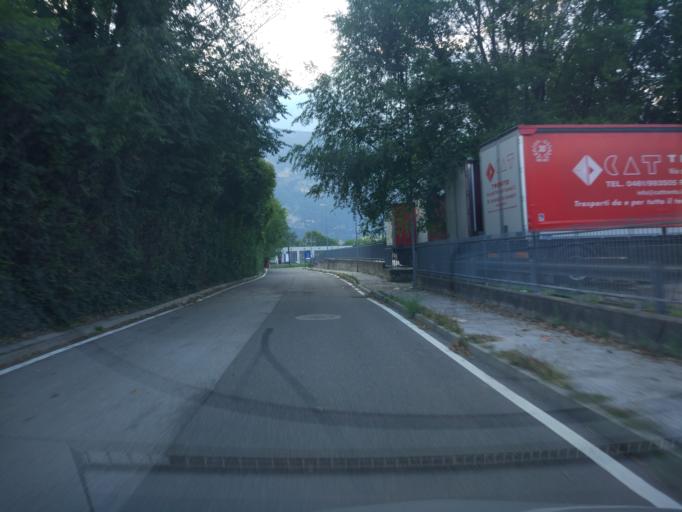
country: IT
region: Trentino-Alto Adige
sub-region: Provincia di Trento
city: Meano
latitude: 46.1205
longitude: 11.1044
